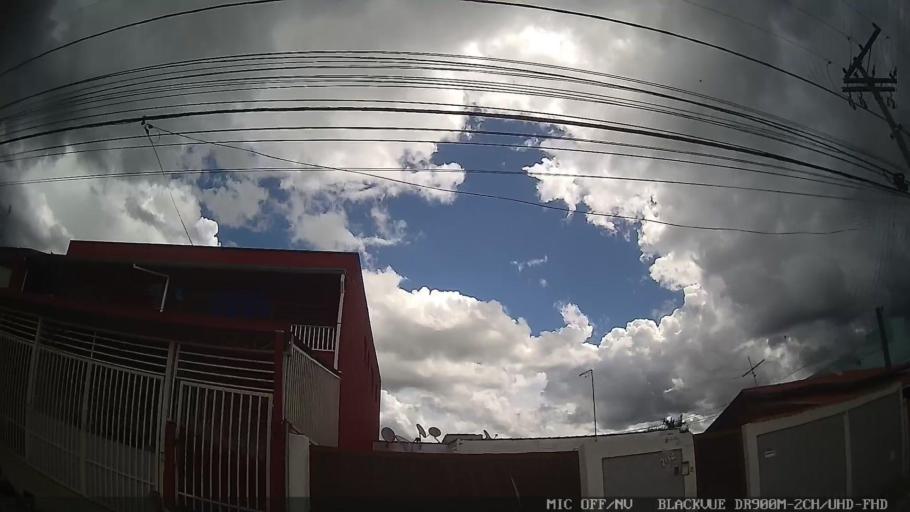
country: BR
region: Sao Paulo
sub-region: Jaguariuna
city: Jaguariuna
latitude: -22.6970
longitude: -47.0008
